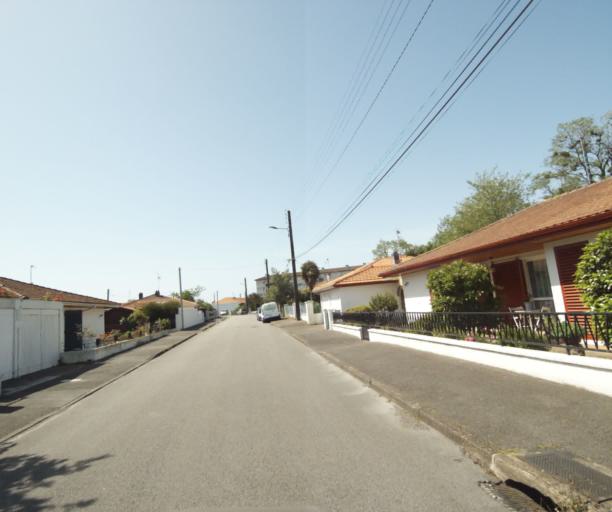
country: FR
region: Aquitaine
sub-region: Departement des Pyrenees-Atlantiques
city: Bayonne
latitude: 43.4781
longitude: -1.4618
